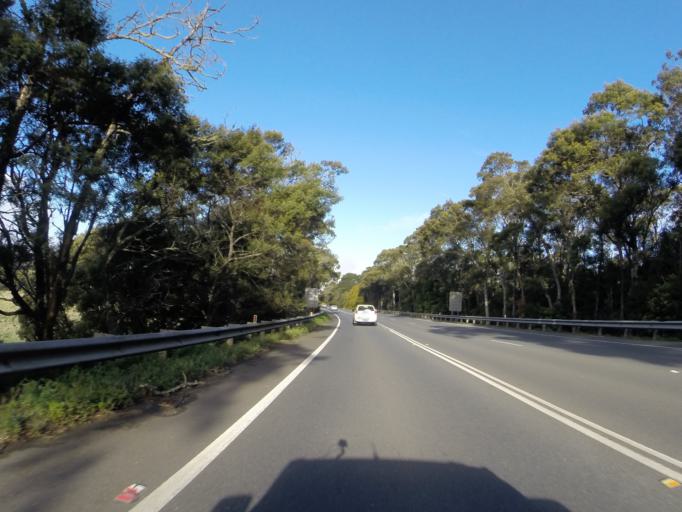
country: AU
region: New South Wales
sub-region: Shoalhaven Shire
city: Kangaroo Valley
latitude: -34.5888
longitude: 150.5631
